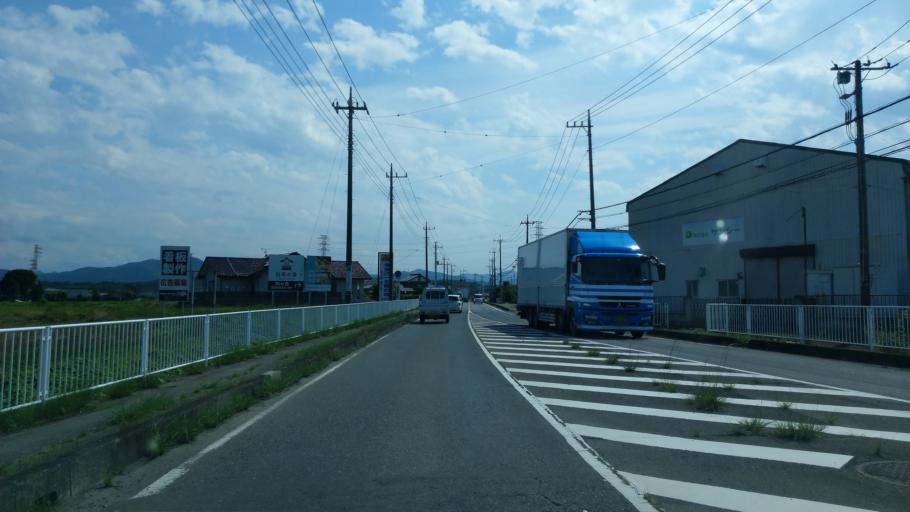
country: JP
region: Saitama
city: Honjo
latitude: 36.2162
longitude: 139.1602
